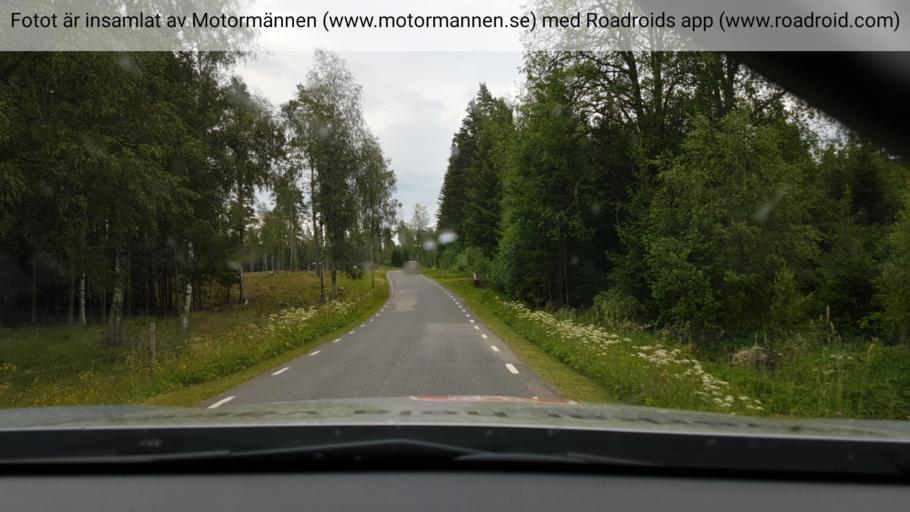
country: SE
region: Joenkoeping
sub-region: Mullsjo Kommun
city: Mullsjoe
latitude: 57.9575
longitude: 13.6871
